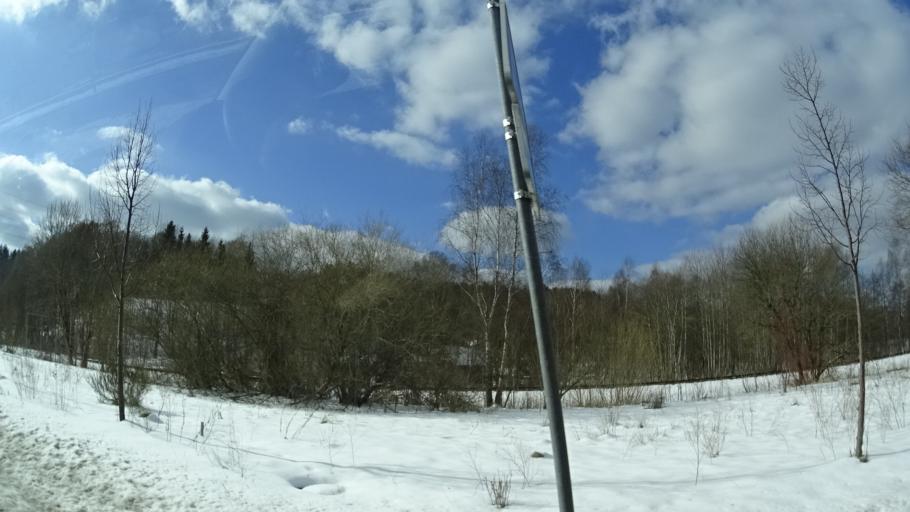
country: DE
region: Thuringia
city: Suhl
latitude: 50.6340
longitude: 10.6980
